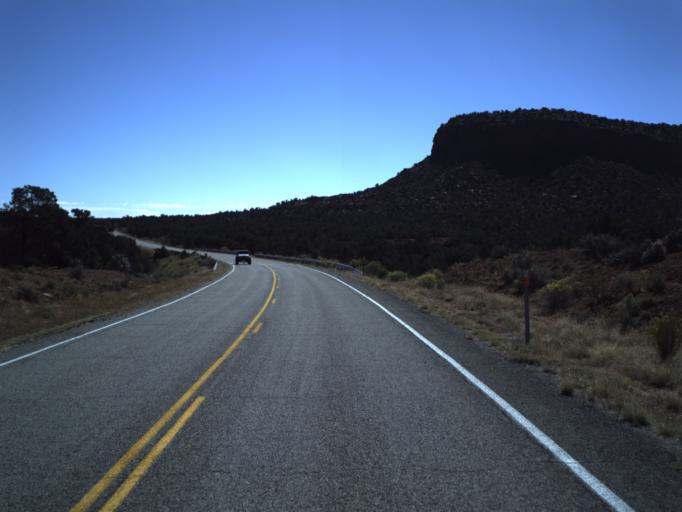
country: US
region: Utah
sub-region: San Juan County
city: Blanding
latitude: 37.5698
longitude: -110.0359
